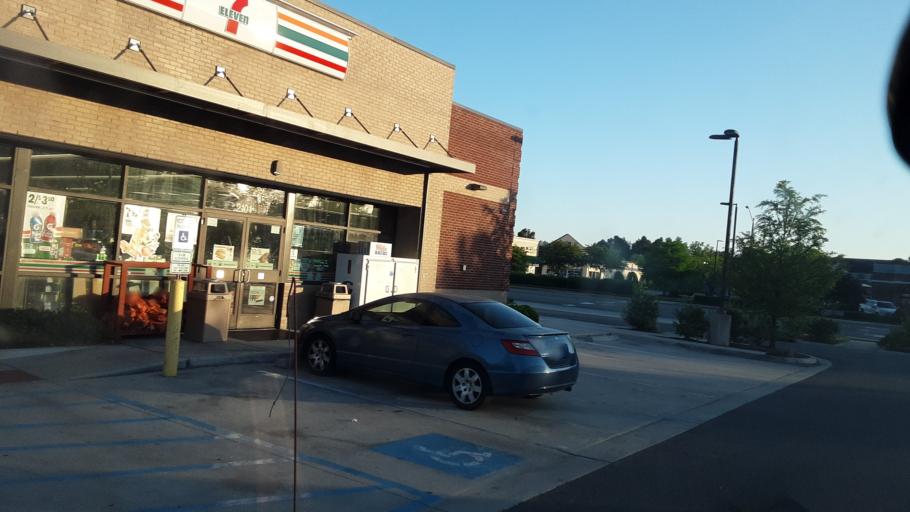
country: US
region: Virginia
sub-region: City of Virginia Beach
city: Virginia Beach
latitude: 36.7682
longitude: -76.0138
